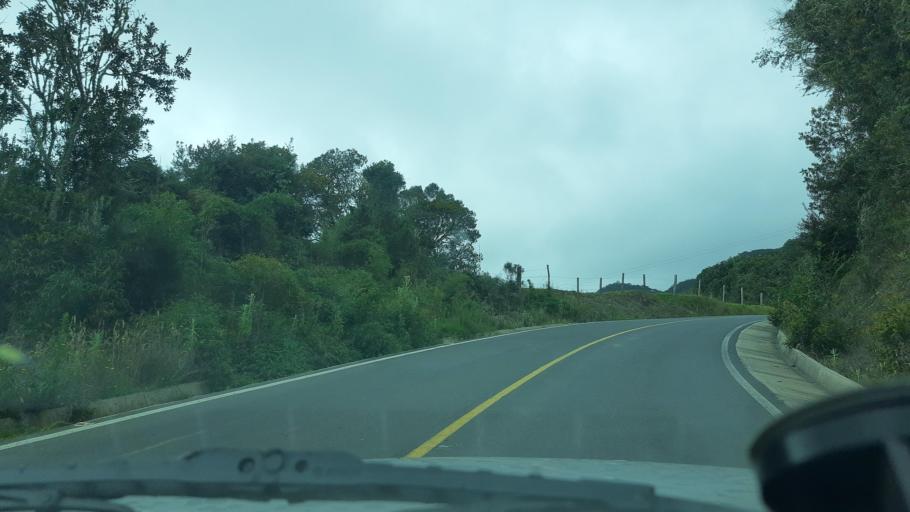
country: CO
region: Cundinamarca
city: Umbita
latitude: 5.2237
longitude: -73.4720
